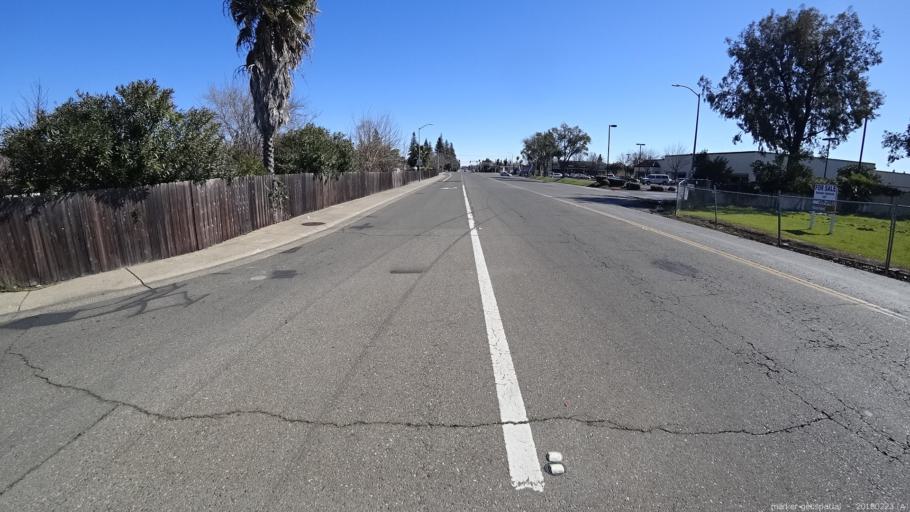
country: US
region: California
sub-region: Sacramento County
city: North Highlands
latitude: 38.7043
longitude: -121.3854
